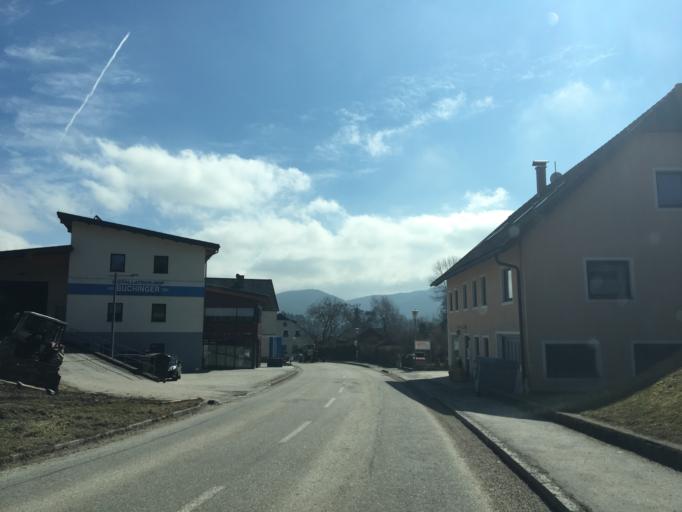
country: AT
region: Lower Austria
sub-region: Politischer Bezirk Melk
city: Nochling
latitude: 48.2751
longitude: 14.9454
